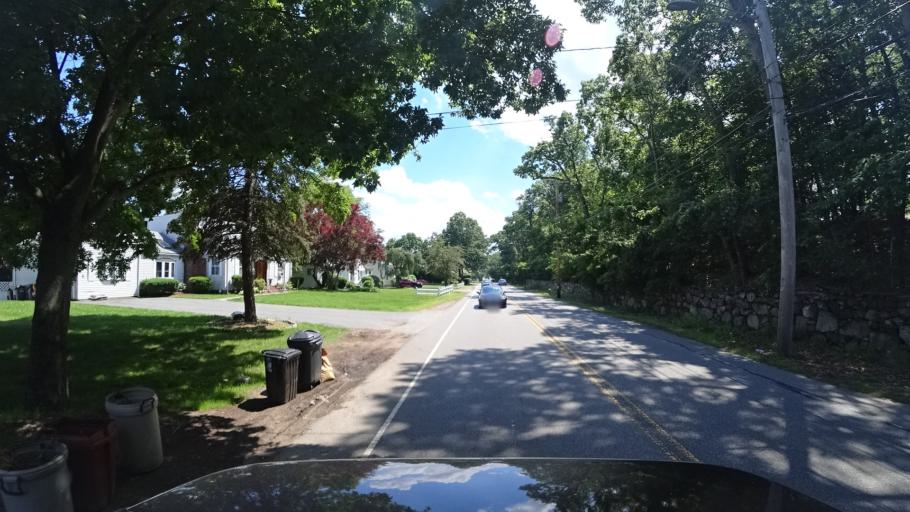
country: US
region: Massachusetts
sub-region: Norfolk County
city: Dedham
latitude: 42.2576
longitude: -71.1791
